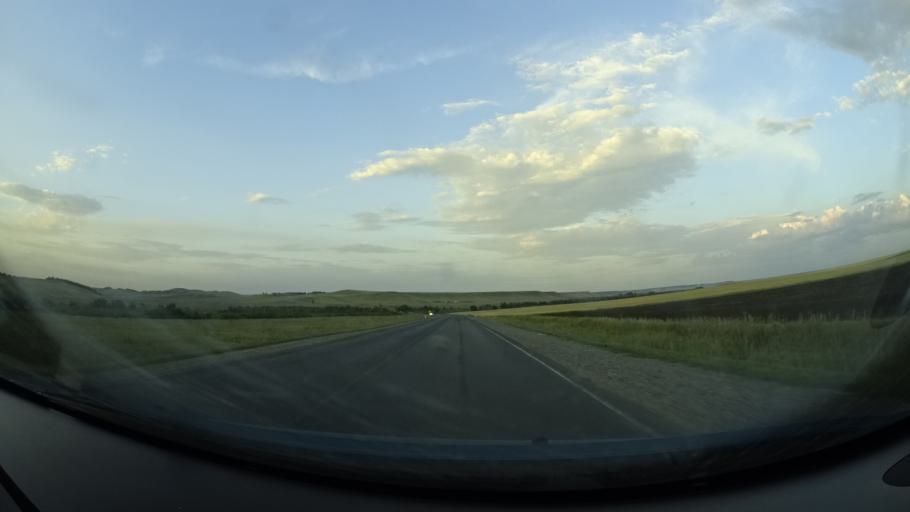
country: RU
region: Orenburg
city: Severnoye
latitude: 54.1297
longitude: 52.5808
